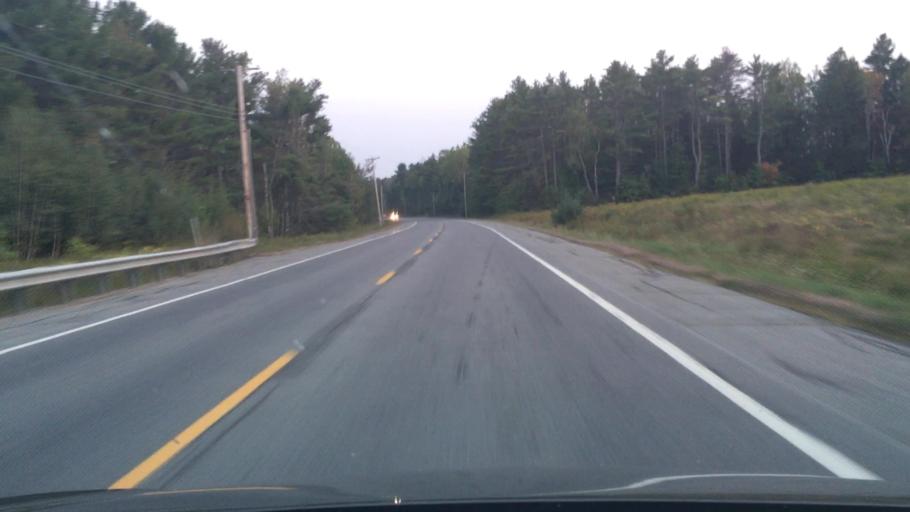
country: US
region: Maine
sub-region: Waldo County
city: Stockton Springs
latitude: 44.5463
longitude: -68.8640
